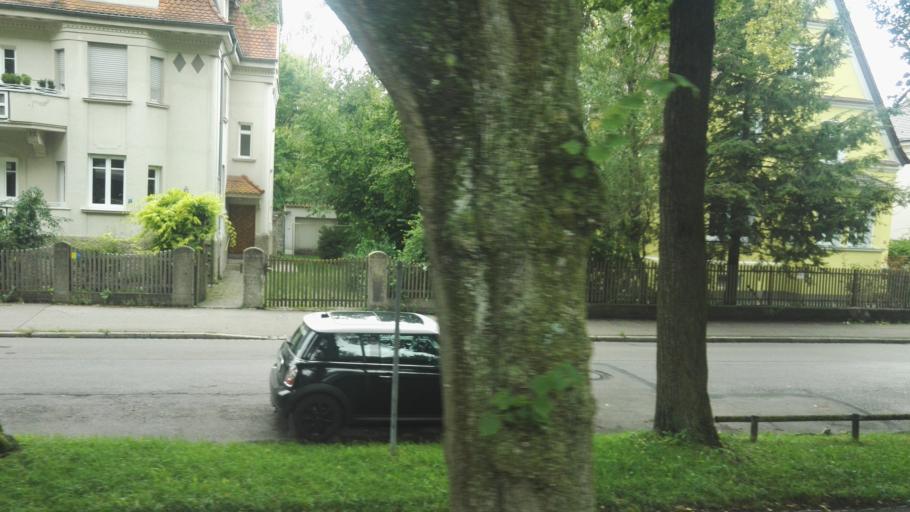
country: DE
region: Bavaria
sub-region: Swabia
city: Augsburg
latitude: 48.3631
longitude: 10.8779
